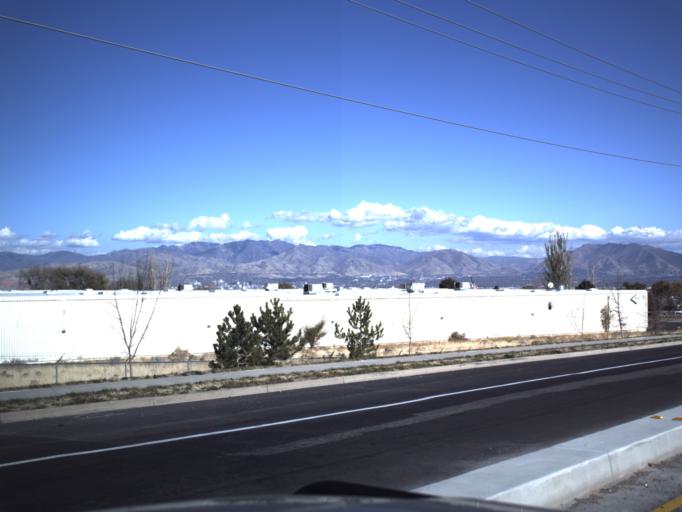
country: US
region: Utah
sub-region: Salt Lake County
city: Kearns
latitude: 40.6675
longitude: -112.0235
